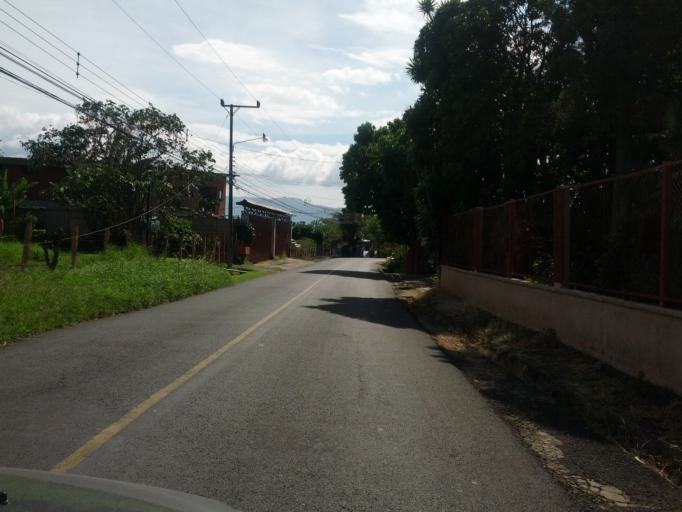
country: CR
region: Heredia
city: Llorente
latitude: 10.0213
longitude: -84.1775
